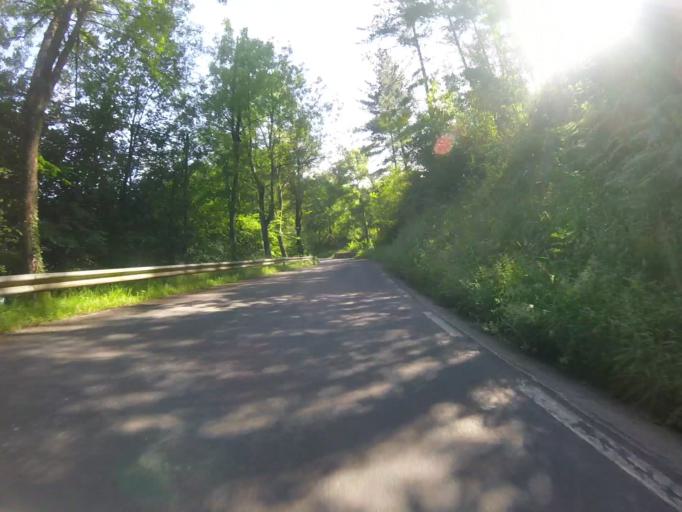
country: ES
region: Basque Country
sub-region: Provincia de Guipuzcoa
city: Ormaiztegui
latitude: 43.0706
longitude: -2.2375
